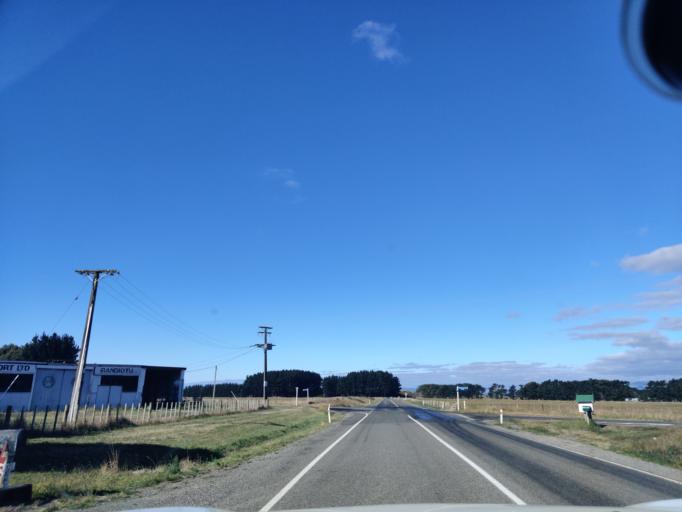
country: NZ
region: Manawatu-Wanganui
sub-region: Horowhenua District
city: Foxton
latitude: -40.4195
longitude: 175.4158
